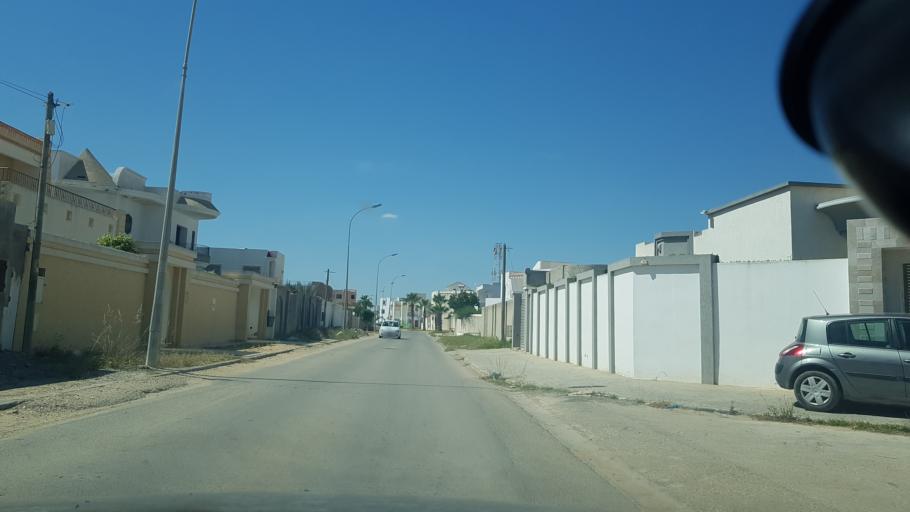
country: TN
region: Safaqis
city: Al Qarmadah
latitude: 34.8241
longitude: 10.7583
